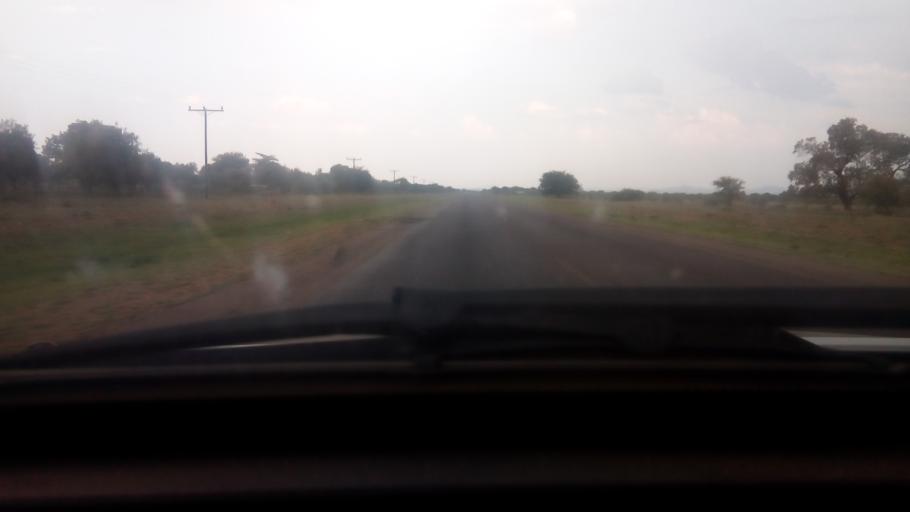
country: BW
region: Kweneng
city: Metsemotlhaba
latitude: -24.4913
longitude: 25.7429
